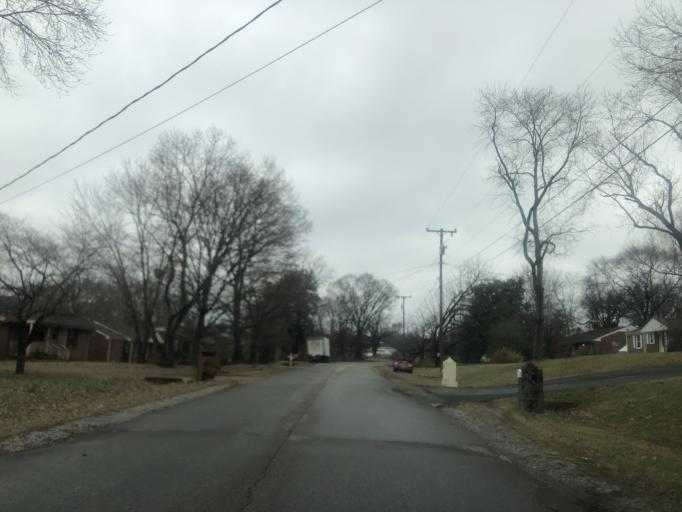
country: US
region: Tennessee
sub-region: Davidson County
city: Lakewood
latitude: 36.1520
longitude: -86.6689
